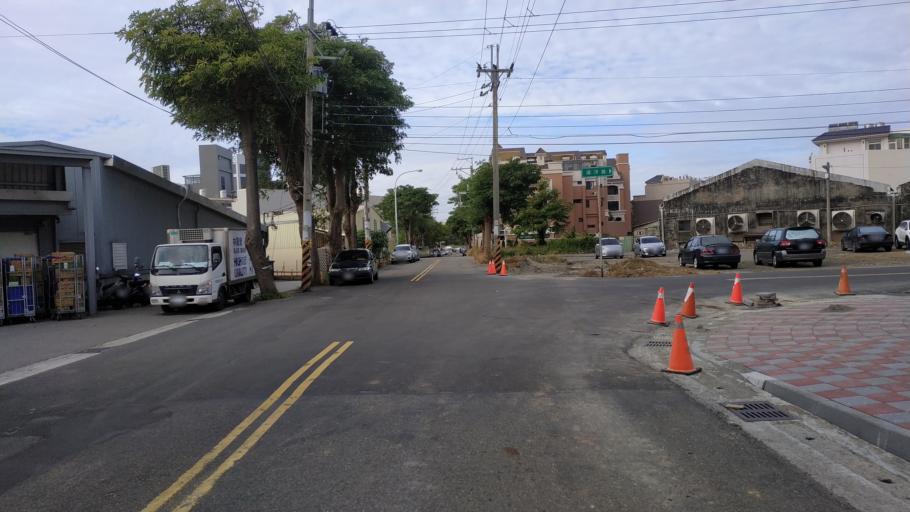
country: TW
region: Taiwan
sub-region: Taichung City
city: Taichung
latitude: 24.2173
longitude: 120.5713
